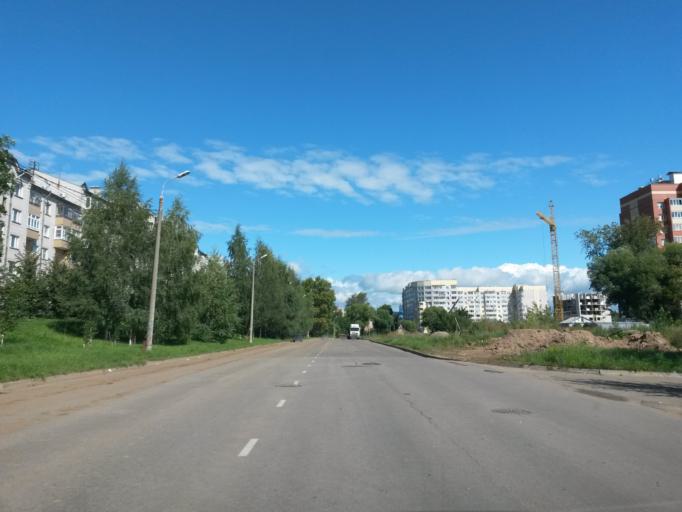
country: RU
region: Jaroslavl
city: Yaroslavl
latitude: 57.5855
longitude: 39.8657
